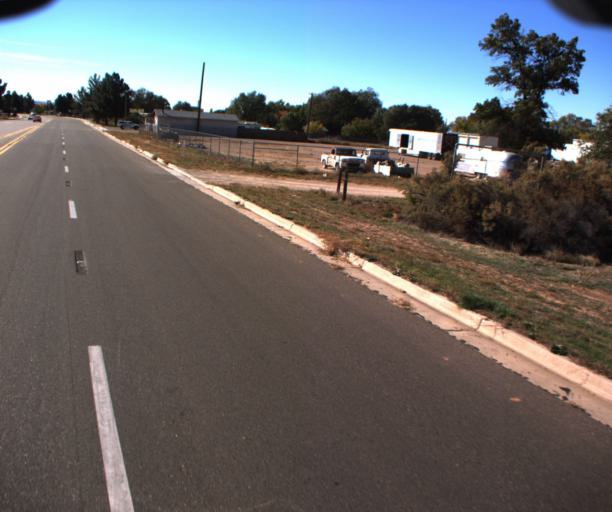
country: US
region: Arizona
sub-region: Coconino County
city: Fredonia
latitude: 36.9589
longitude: -112.5270
